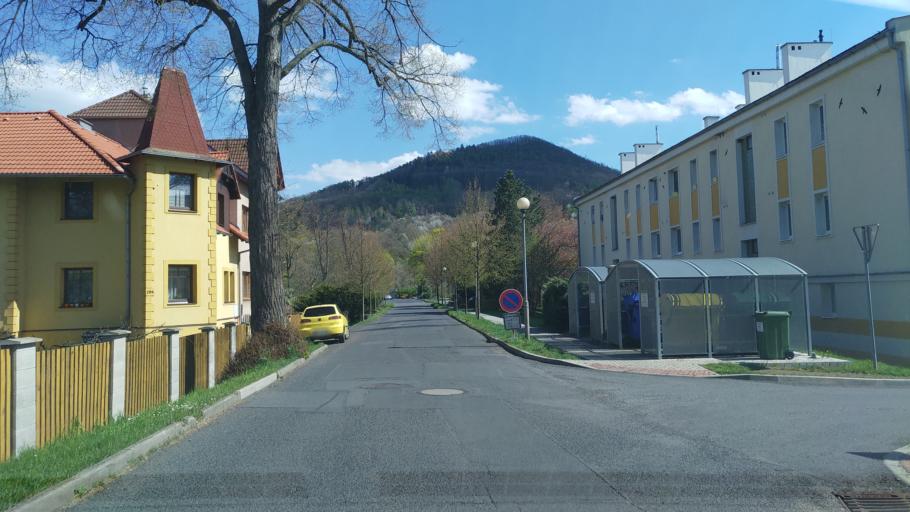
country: CZ
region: Ustecky
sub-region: Okres Chomutov
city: Klasterec nad Ohri
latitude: 50.3809
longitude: 13.1708
